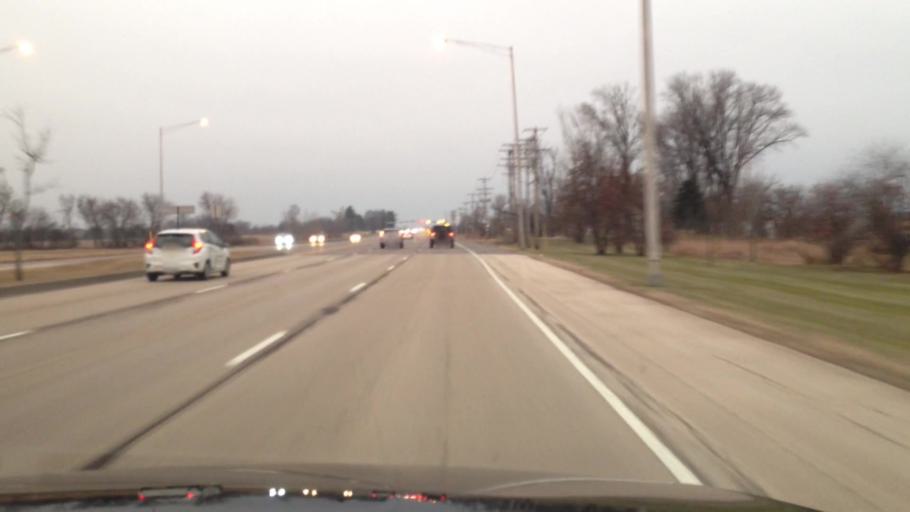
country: US
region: Illinois
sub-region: McHenry County
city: Lake in the Hills
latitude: 42.1455
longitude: -88.3360
